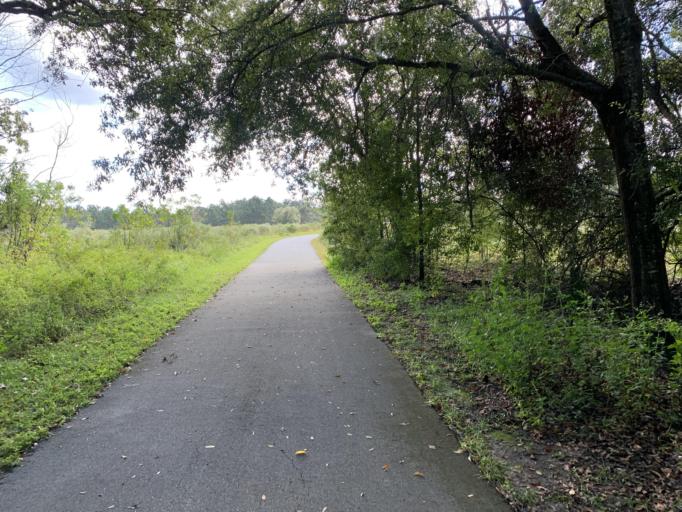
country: US
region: Florida
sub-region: Marion County
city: Silver Springs Shores
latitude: 29.1564
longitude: -82.0450
